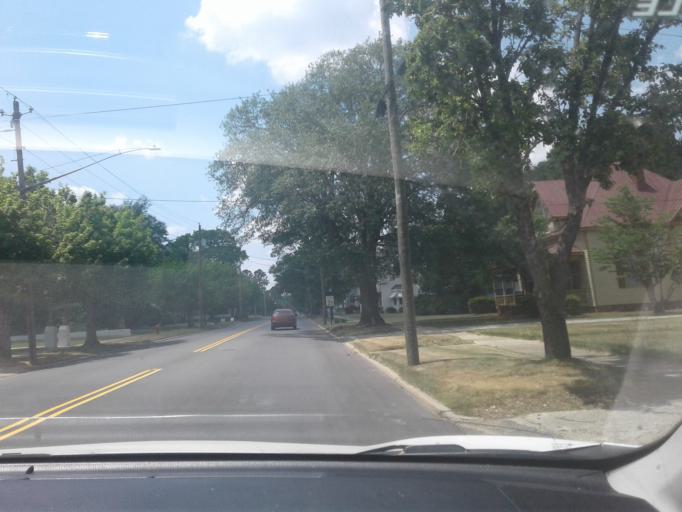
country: US
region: North Carolina
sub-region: Johnston County
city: Benson
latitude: 35.3835
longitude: -78.5513
